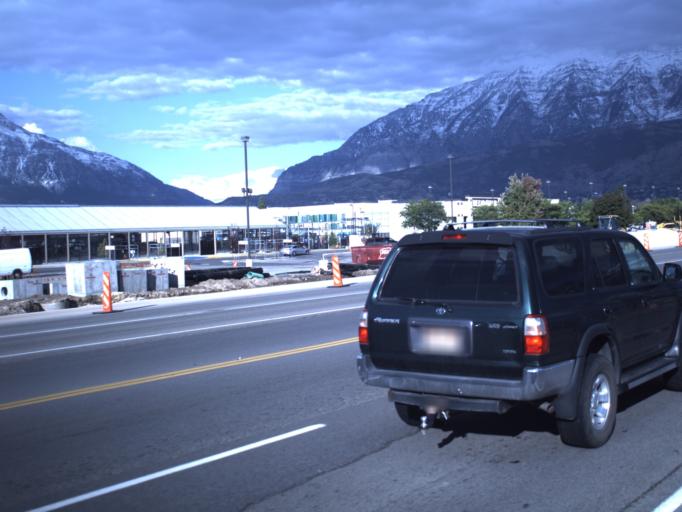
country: US
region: Utah
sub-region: Utah County
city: Orem
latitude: 40.2735
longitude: -111.6981
